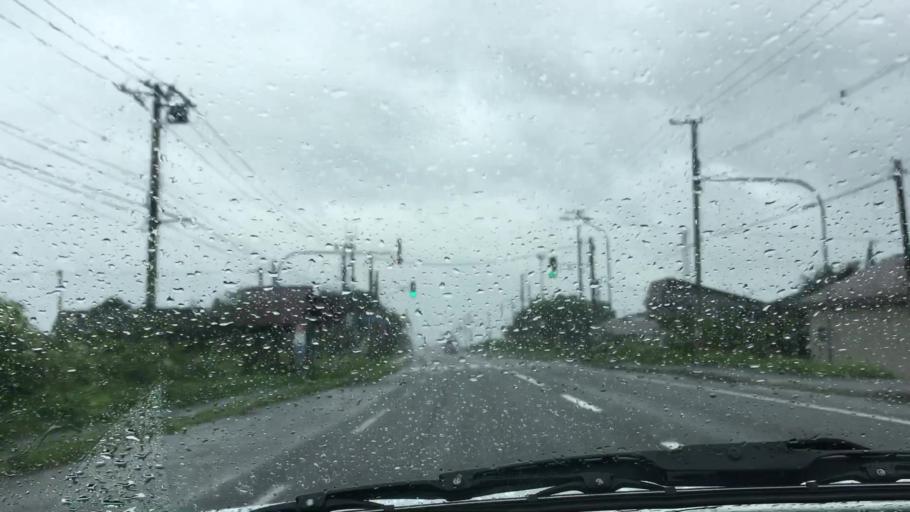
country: JP
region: Hokkaido
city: Nanae
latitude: 42.3150
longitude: 140.2739
